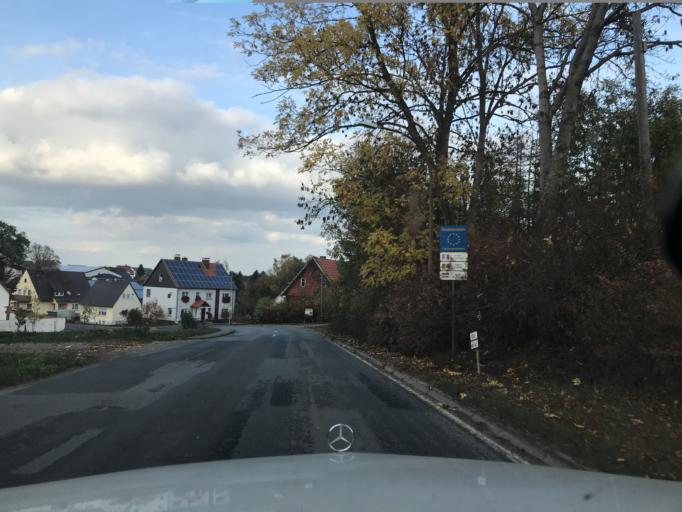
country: DE
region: Hesse
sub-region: Regierungsbezirk Kassel
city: Calden
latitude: 51.4317
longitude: 9.3816
